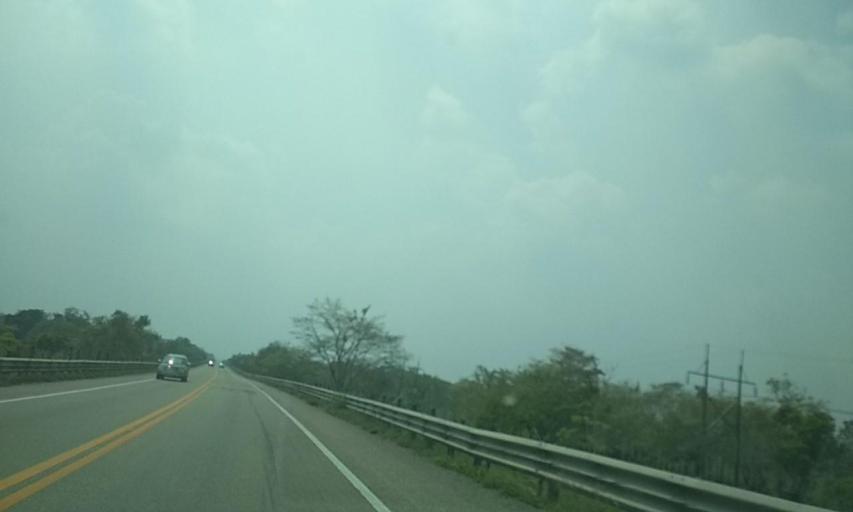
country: MX
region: Tabasco
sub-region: Huimanguillo
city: Francisco Rueda
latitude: 17.7617
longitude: -94.0114
